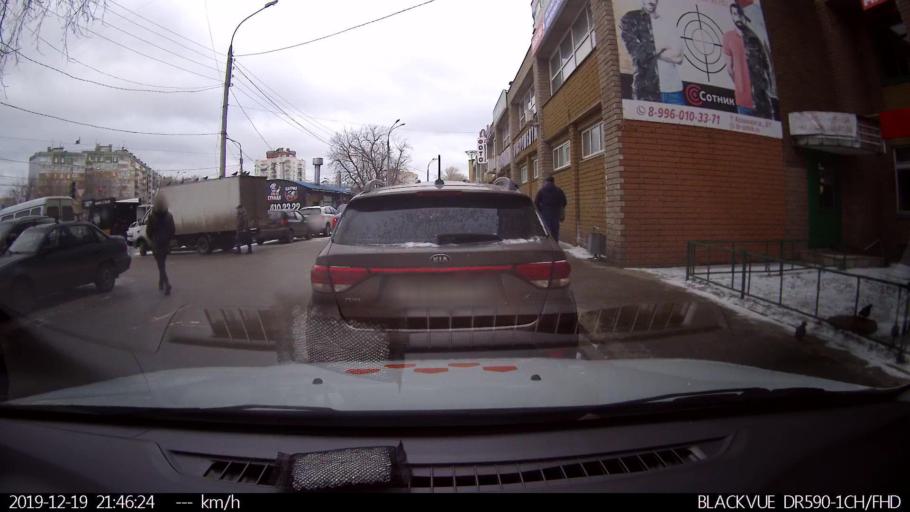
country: RU
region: Nizjnij Novgorod
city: Afonino
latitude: 56.2675
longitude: 44.0595
